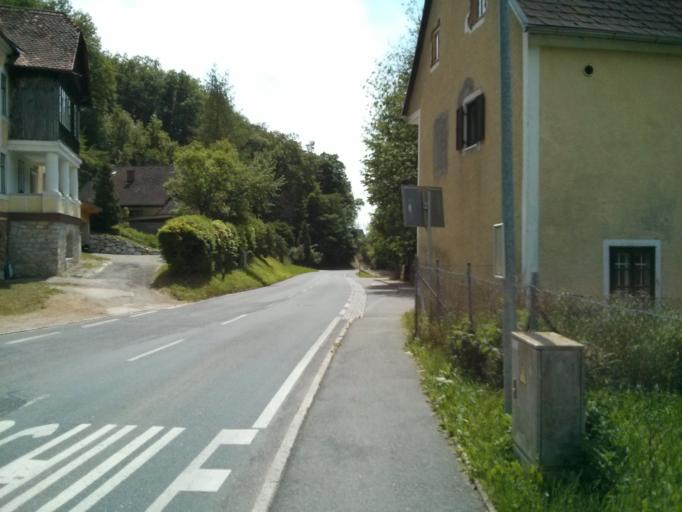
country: AT
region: Styria
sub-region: Politischer Bezirk Graz-Umgebung
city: Stattegg
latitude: 47.1454
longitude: 15.4185
